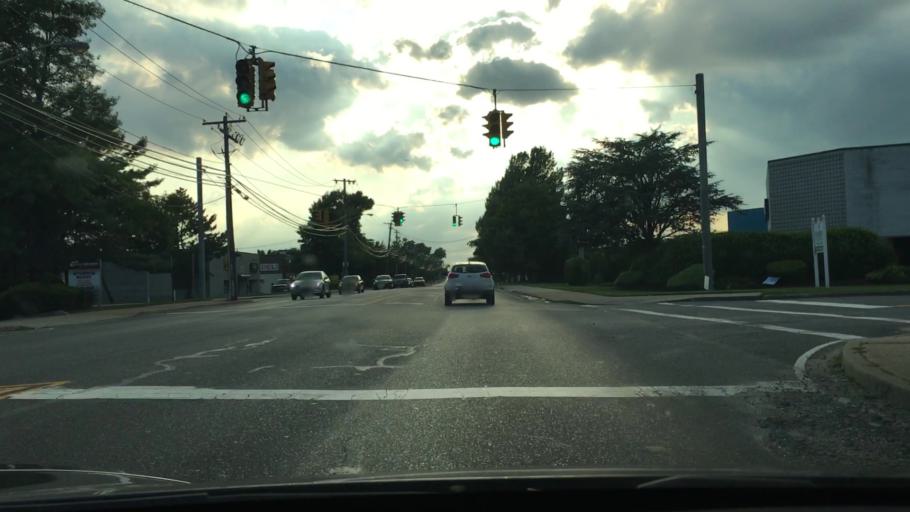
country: US
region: New York
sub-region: Suffolk County
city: Bay Wood
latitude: 40.7611
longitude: -73.2983
